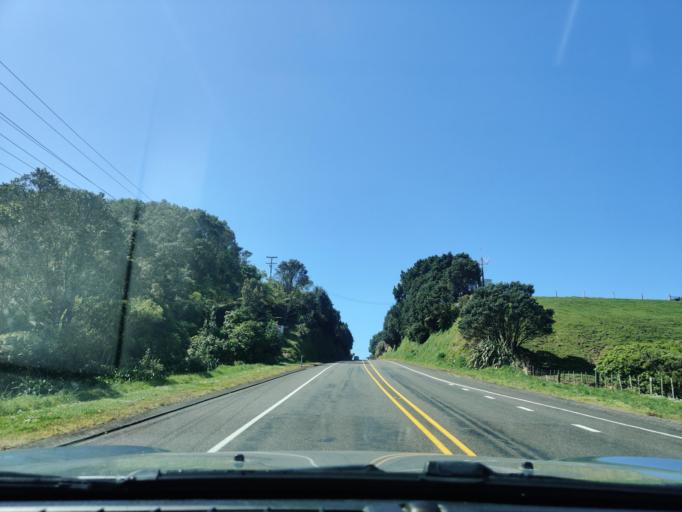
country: NZ
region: Taranaki
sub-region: New Plymouth District
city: New Plymouth
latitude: -39.1111
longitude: 173.9598
